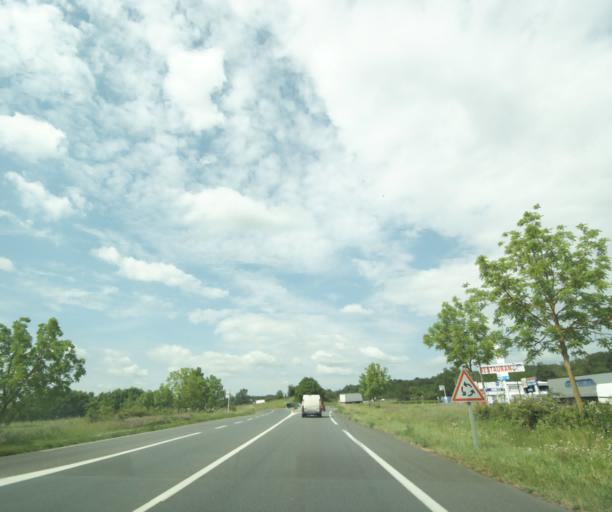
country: FR
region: Pays de la Loire
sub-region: Departement de Maine-et-Loire
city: Distre
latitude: 47.2338
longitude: -0.1122
